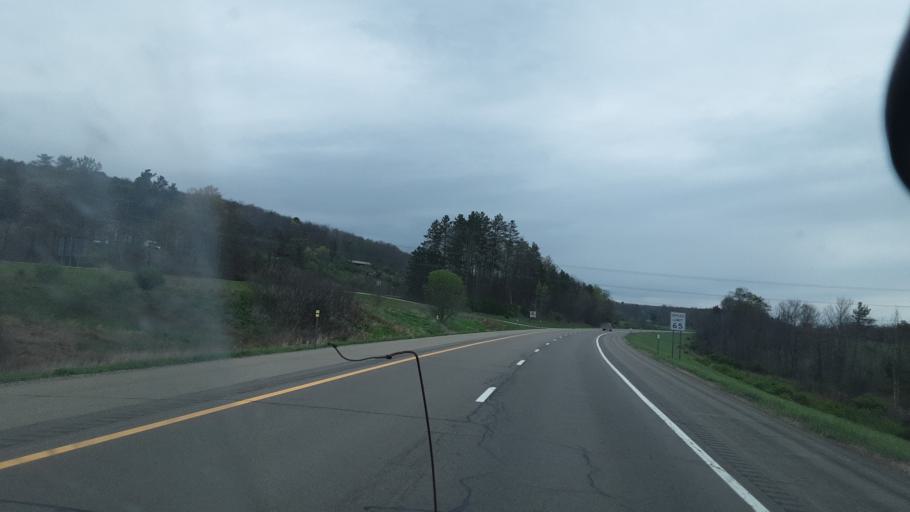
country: US
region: New York
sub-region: Allegany County
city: Friendship
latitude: 42.2154
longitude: -78.1390
